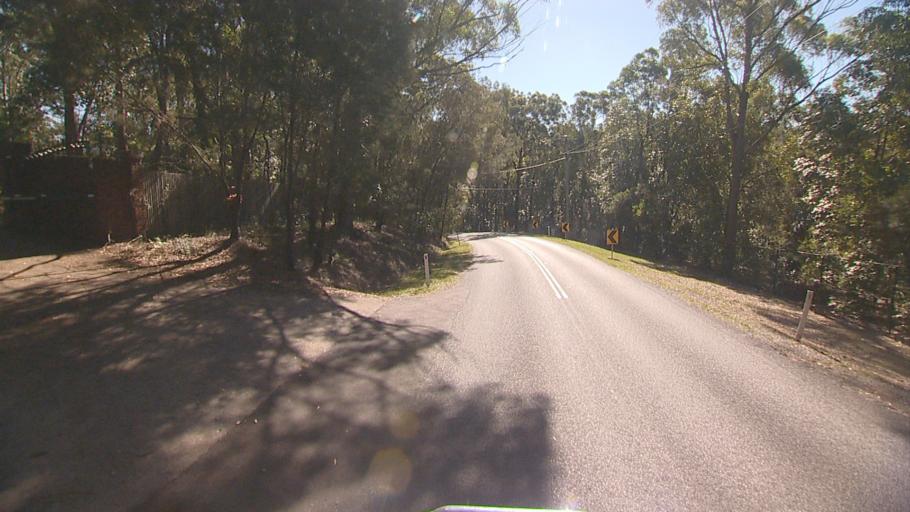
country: AU
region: Queensland
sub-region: Logan
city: Springwood
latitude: -27.5983
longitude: 153.1642
